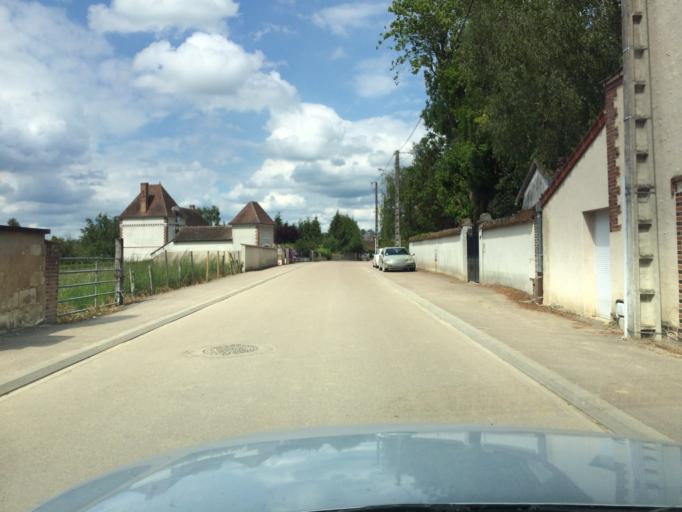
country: FR
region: Bourgogne
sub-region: Departement de l'Yonne
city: Fleury-la-Vallee
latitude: 47.8943
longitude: 3.4408
